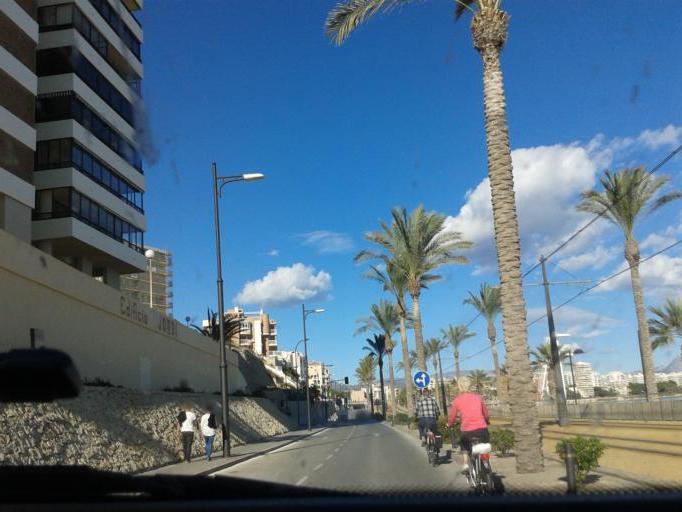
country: ES
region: Valencia
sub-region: Provincia de Alicante
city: el Campello
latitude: 38.4070
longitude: -0.4036
